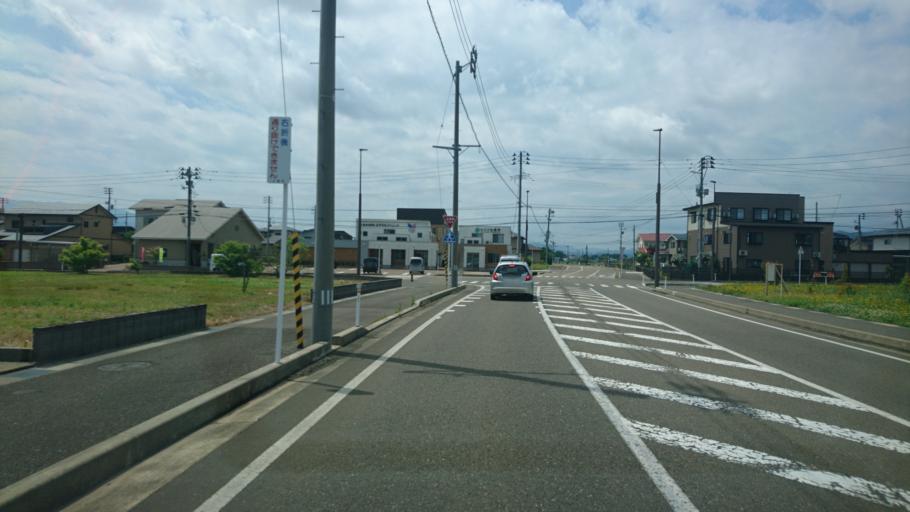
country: JP
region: Niigata
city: Joetsu
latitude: 37.0791
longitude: 138.2470
